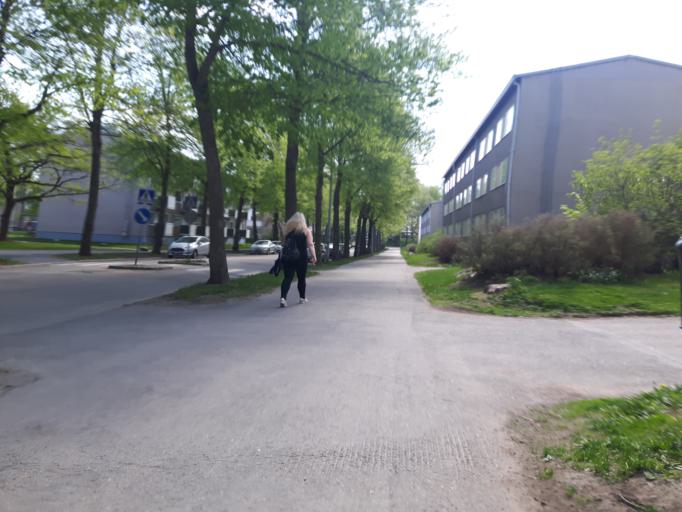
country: FI
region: Uusimaa
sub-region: Helsinki
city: Vantaa
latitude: 60.2131
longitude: 25.1027
